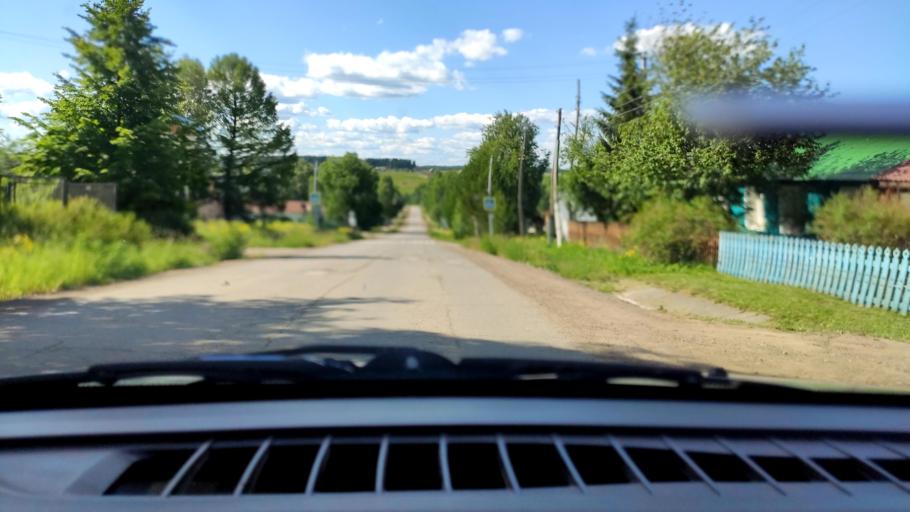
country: RU
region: Perm
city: Uinskoye
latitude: 57.1136
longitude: 56.5300
